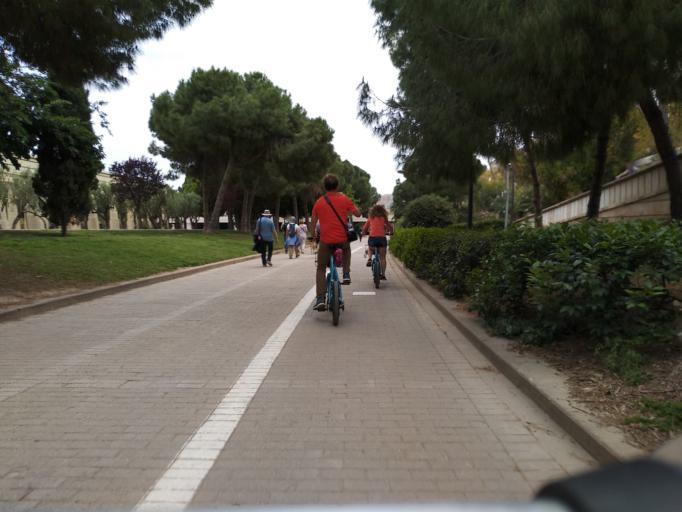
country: ES
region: Valencia
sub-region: Provincia de Valencia
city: Valencia
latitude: 39.4645
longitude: -0.3611
